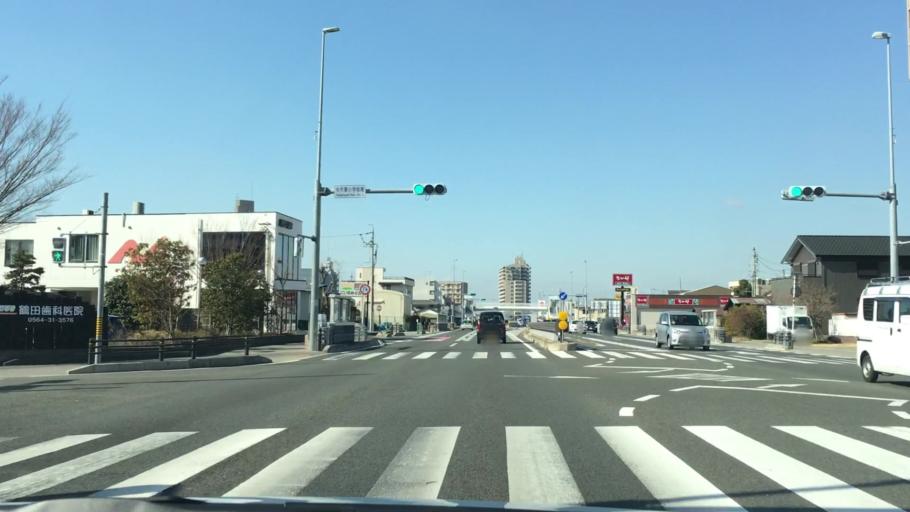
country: JP
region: Aichi
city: Okazaki
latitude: 34.9612
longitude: 137.1440
